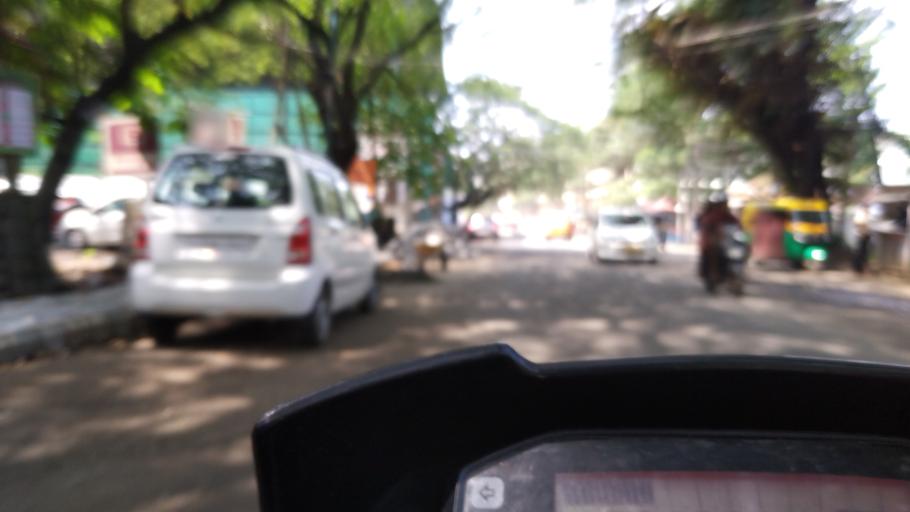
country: IN
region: Kerala
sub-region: Ernakulam
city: Cochin
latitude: 9.9673
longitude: 76.2986
